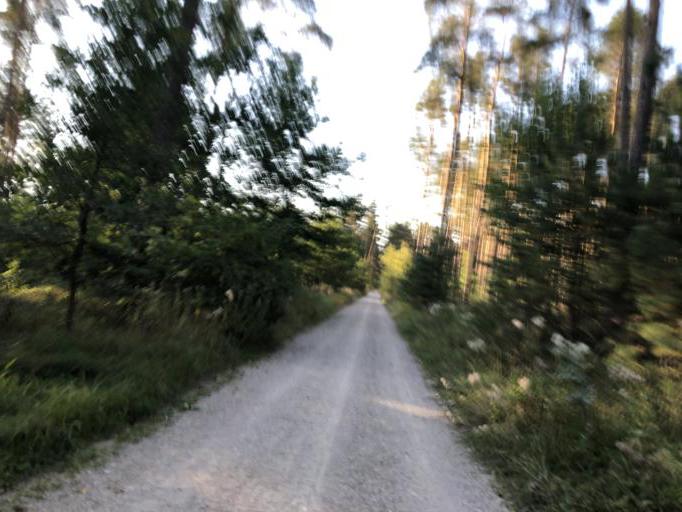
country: DE
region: Bavaria
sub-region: Regierungsbezirk Mittelfranken
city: Uttenreuth
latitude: 49.5794
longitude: 11.0714
